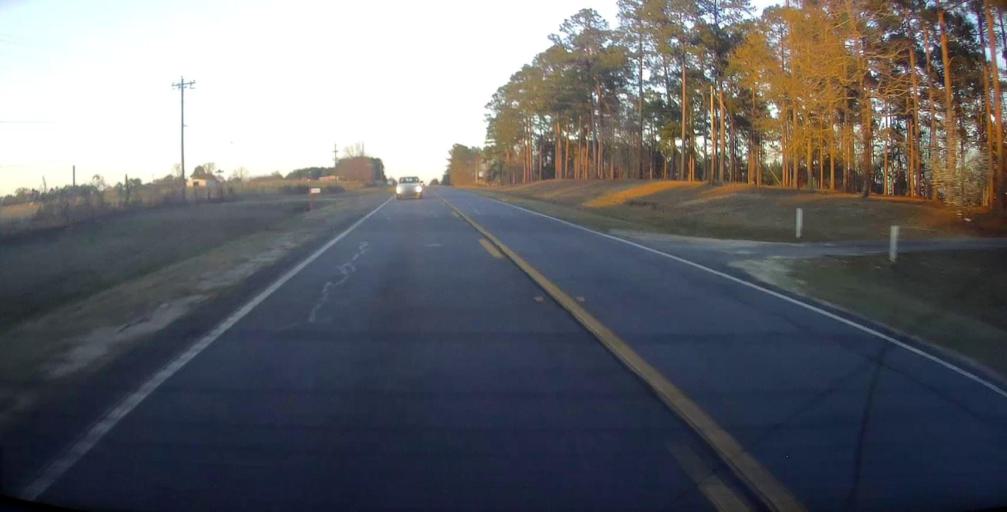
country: US
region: Georgia
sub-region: Dodge County
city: Eastman
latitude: 32.2469
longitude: -83.1440
